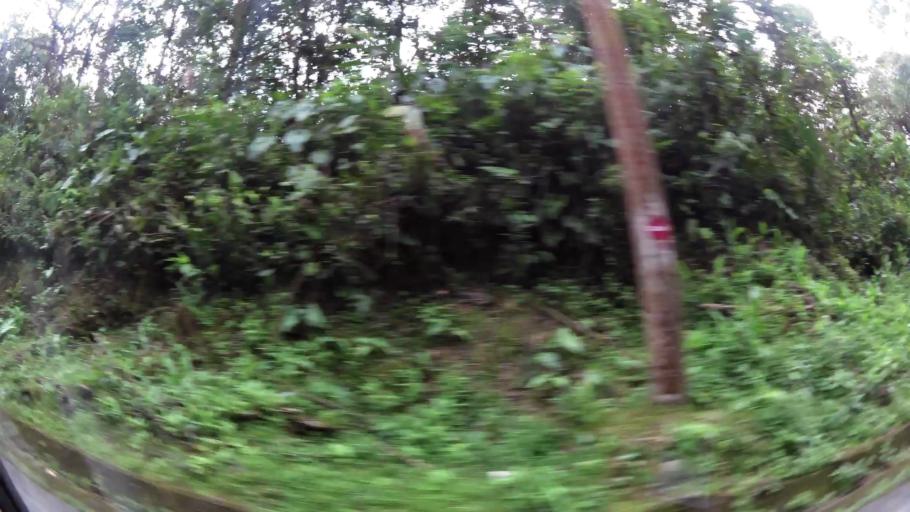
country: EC
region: Pastaza
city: Puyo
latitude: -1.4260
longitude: -78.1764
